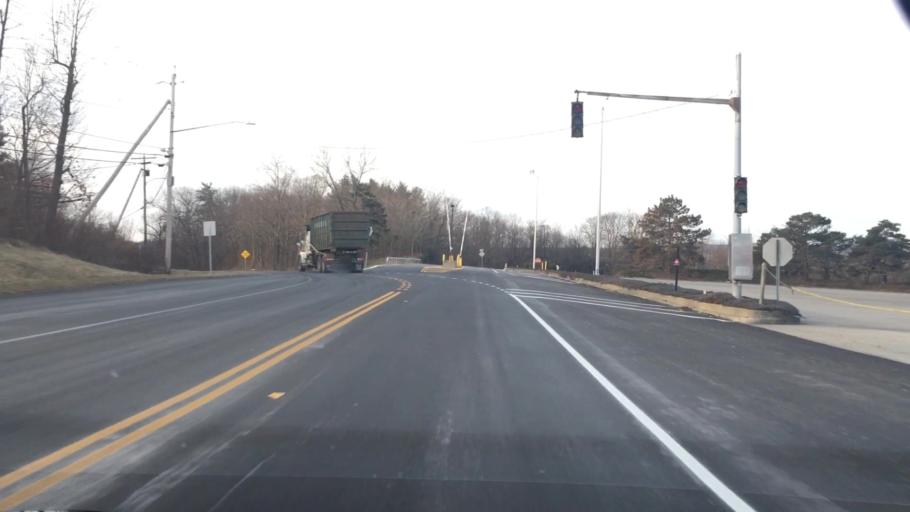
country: US
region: New York
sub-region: Dutchess County
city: Crown Heights
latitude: 41.6498
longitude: -73.9376
